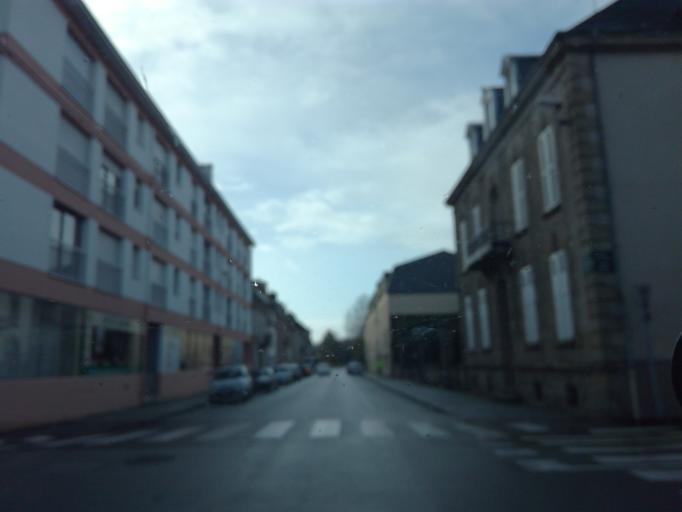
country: FR
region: Brittany
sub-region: Departement du Morbihan
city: Pontivy
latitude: 48.0613
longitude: -2.9674
